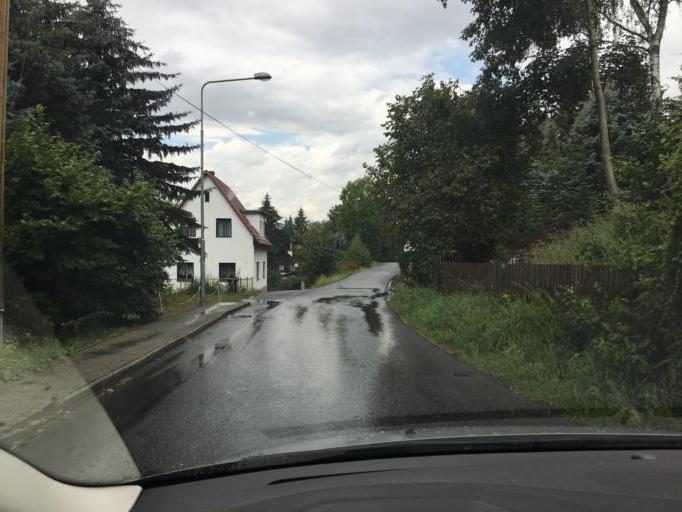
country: CZ
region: Ustecky
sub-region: Okres Decin
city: Decin
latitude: 50.8487
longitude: 14.2888
